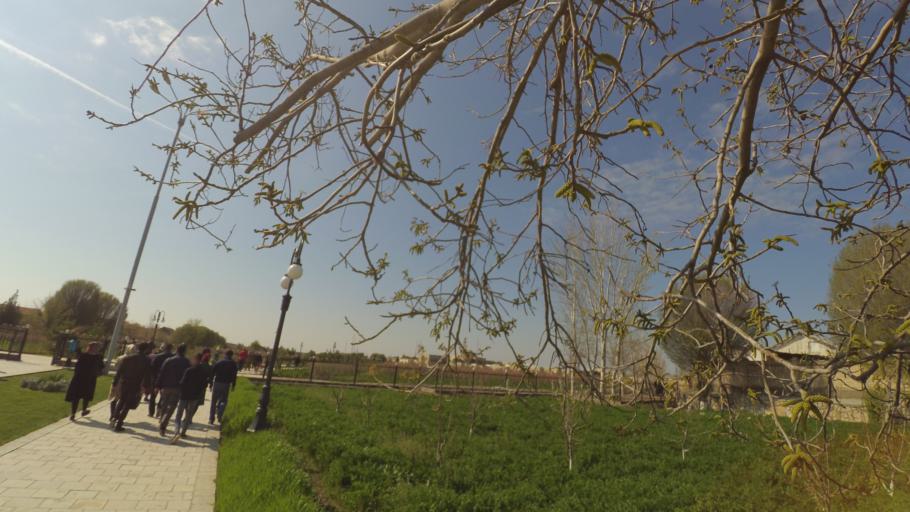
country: UZ
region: Bukhara
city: Kogon
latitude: 39.8050
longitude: 64.5401
